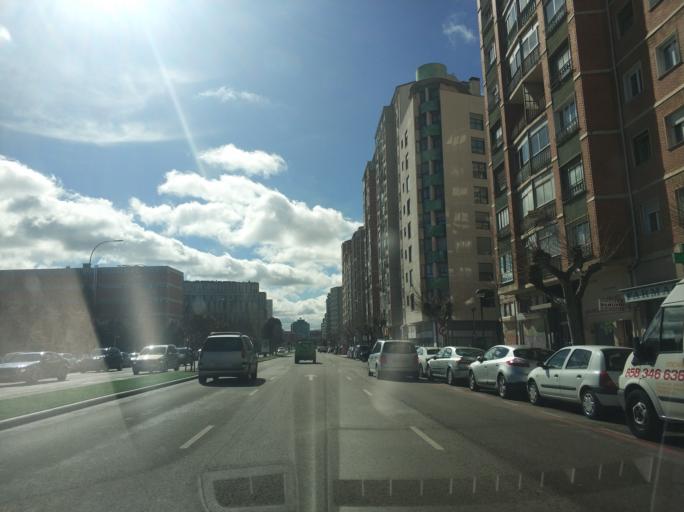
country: ES
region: Castille and Leon
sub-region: Provincia de Burgos
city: Burgos
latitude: 42.3522
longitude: -3.6904
